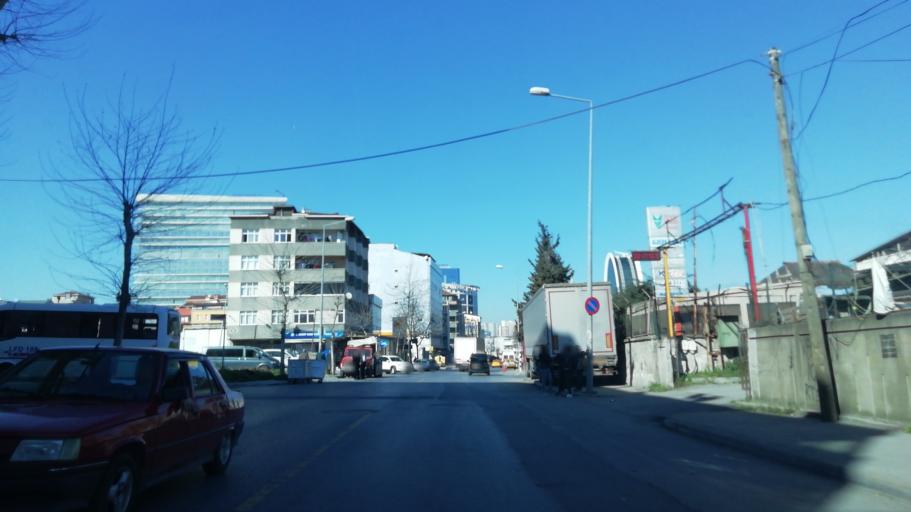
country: TR
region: Istanbul
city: Mahmutbey
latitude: 41.0236
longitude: 28.8063
